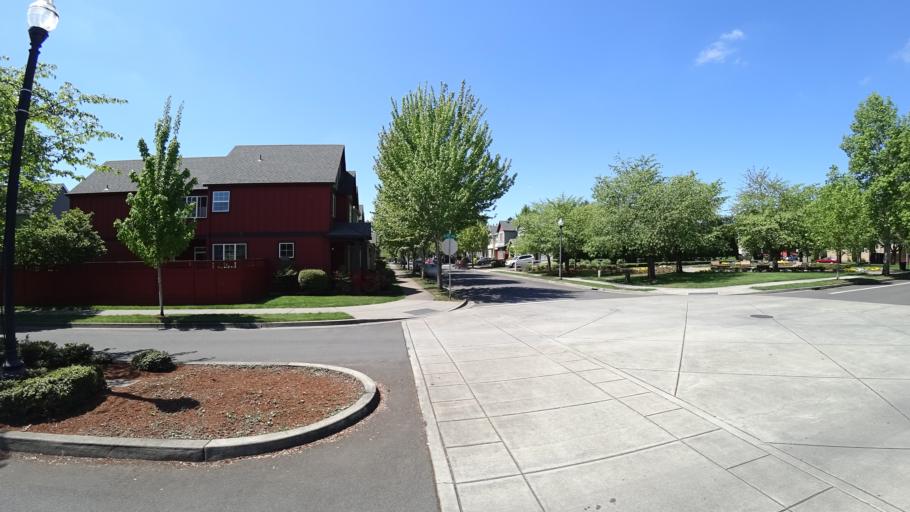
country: US
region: Oregon
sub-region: Washington County
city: Hillsboro
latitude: 45.5097
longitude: -122.9740
